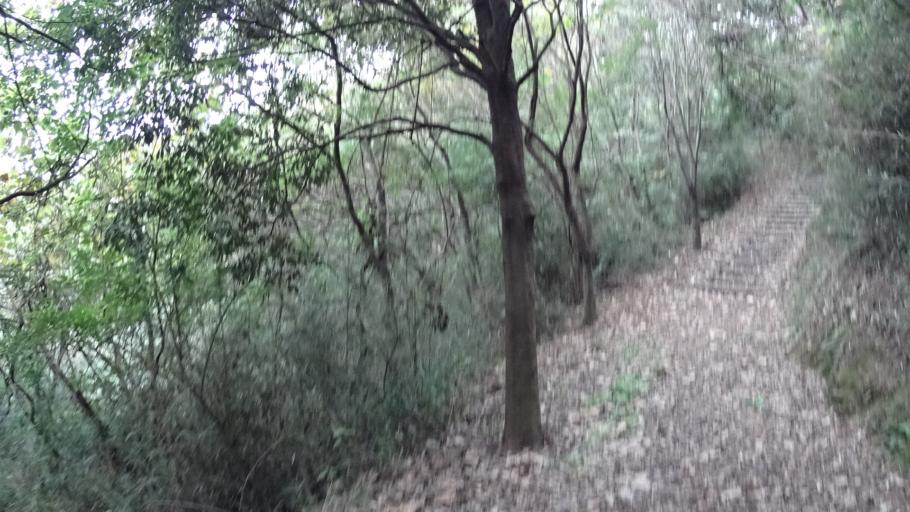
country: JP
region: Kanagawa
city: Zushi
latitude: 35.2896
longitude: 139.6143
